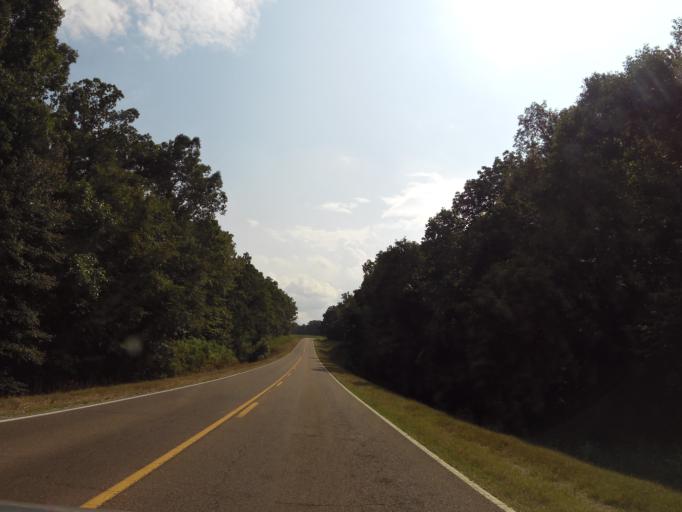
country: US
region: Tennessee
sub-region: Hardin County
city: Crump
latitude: 35.1468
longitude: -88.3506
